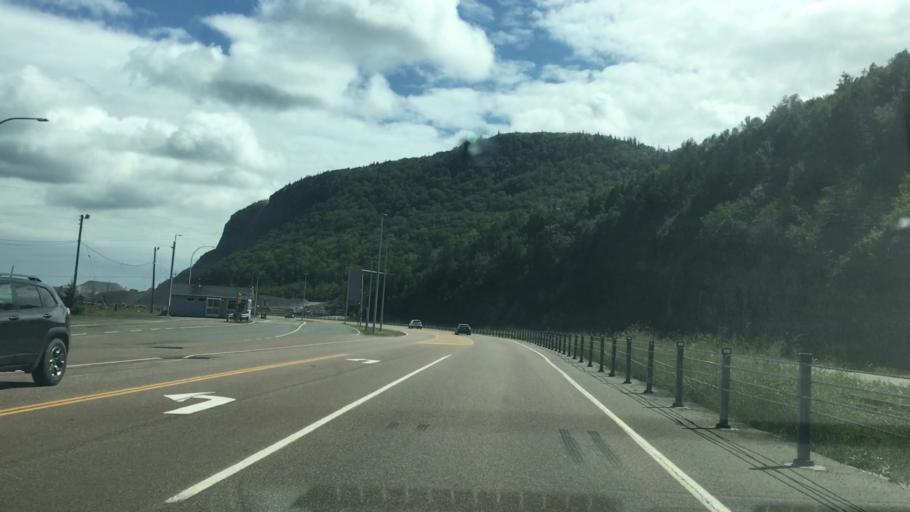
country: CA
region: Nova Scotia
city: Port Hawkesbury
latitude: 45.6425
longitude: -61.4304
